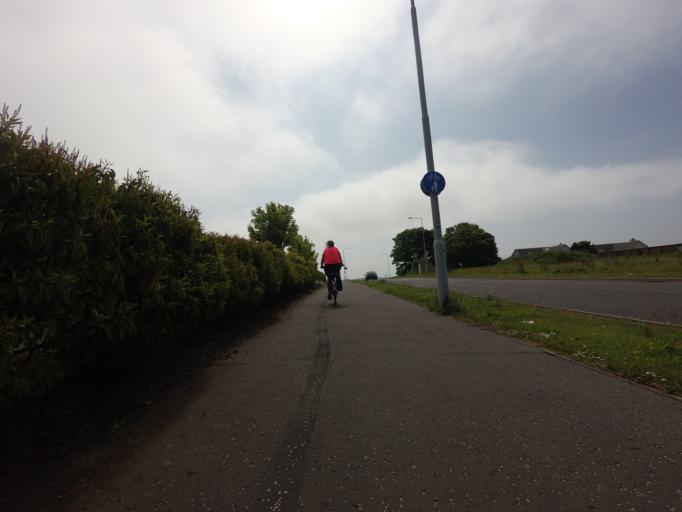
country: GB
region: Scotland
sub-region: Fife
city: Inverkeithing
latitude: 56.0502
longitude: -3.4109
